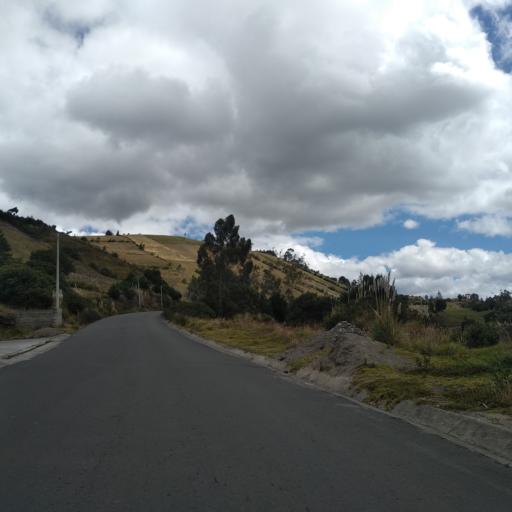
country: EC
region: Cotopaxi
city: Saquisili
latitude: -0.7502
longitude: -78.7232
